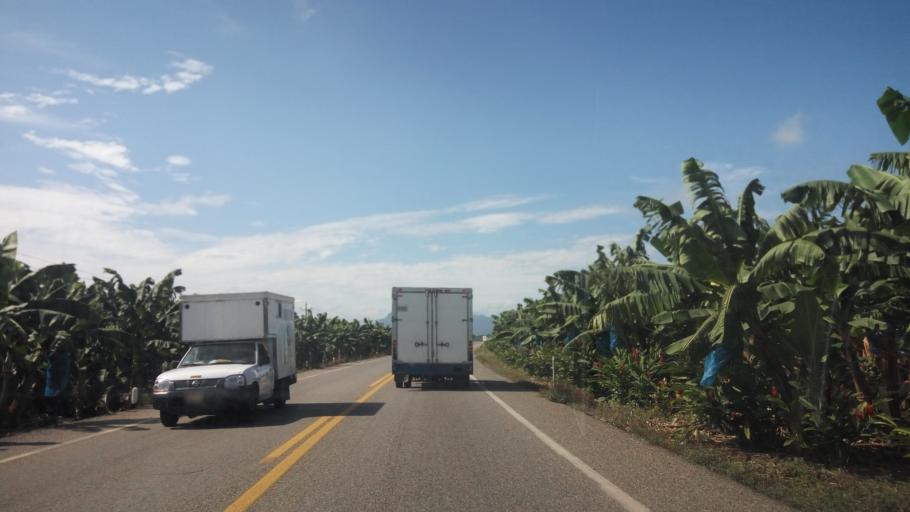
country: MX
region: Tabasco
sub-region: Teapa
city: Eureka y Belen
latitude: 17.6455
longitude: -92.9654
